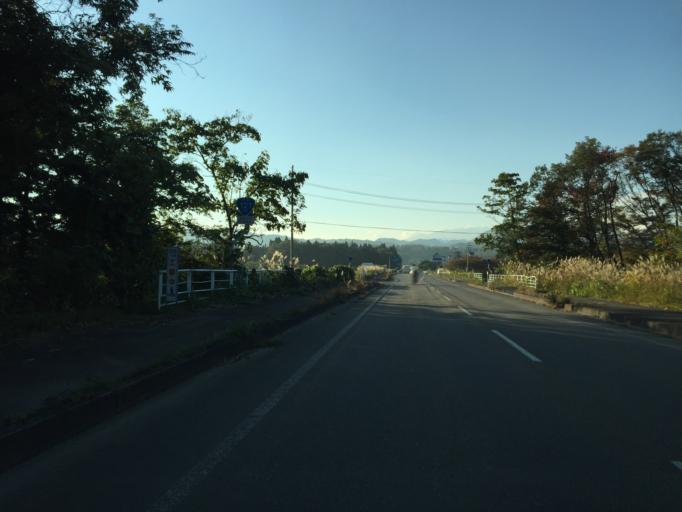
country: JP
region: Fukushima
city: Kitakata
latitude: 37.6990
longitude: 139.8811
